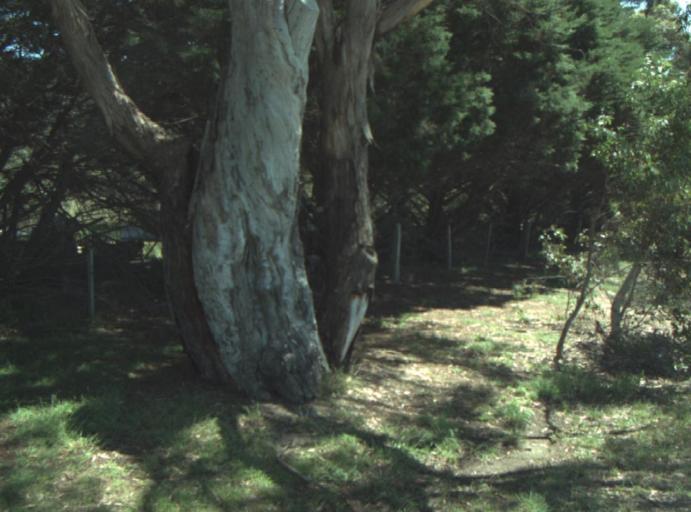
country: AU
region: Victoria
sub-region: Greater Geelong
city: Lara
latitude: -37.8566
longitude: 144.2808
